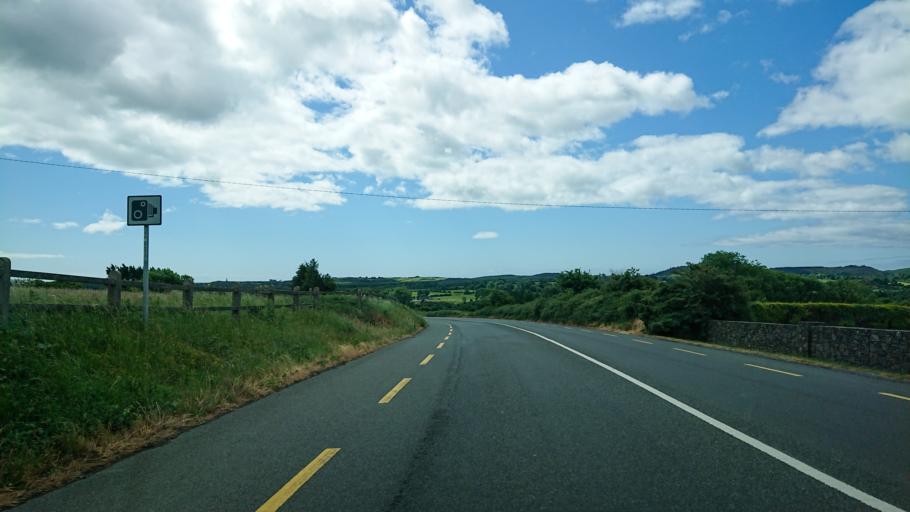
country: IE
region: Munster
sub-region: Waterford
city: Tra Mhor
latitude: 52.2012
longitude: -7.1947
